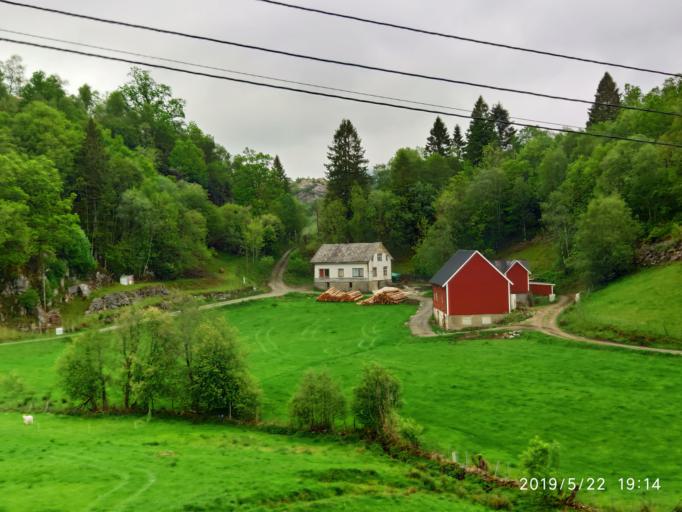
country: NO
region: Hordaland
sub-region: Tysnes
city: Uggdal
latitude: 59.9531
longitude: 5.4892
